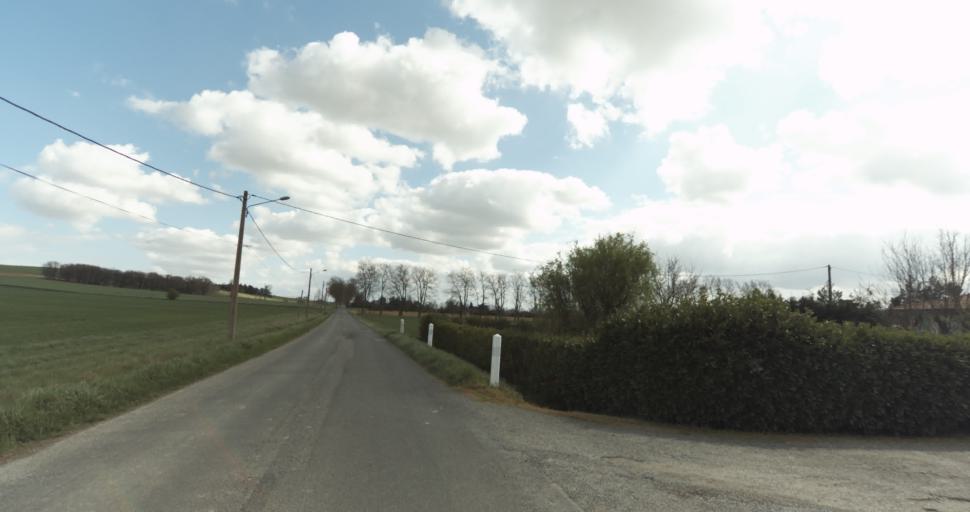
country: FR
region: Midi-Pyrenees
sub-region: Departement de la Haute-Garonne
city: Auterive
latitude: 43.3761
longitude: 1.4639
